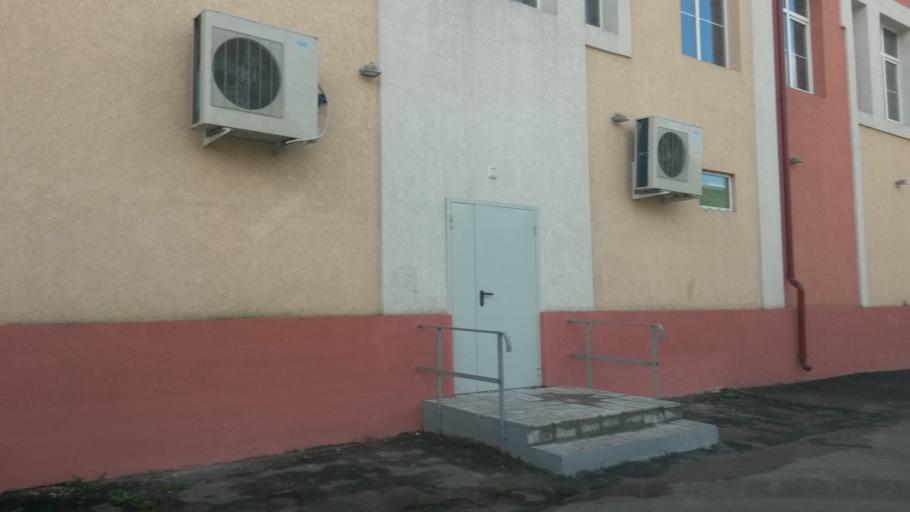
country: RU
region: Ivanovo
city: Zavolzhsk
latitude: 57.4910
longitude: 42.1358
